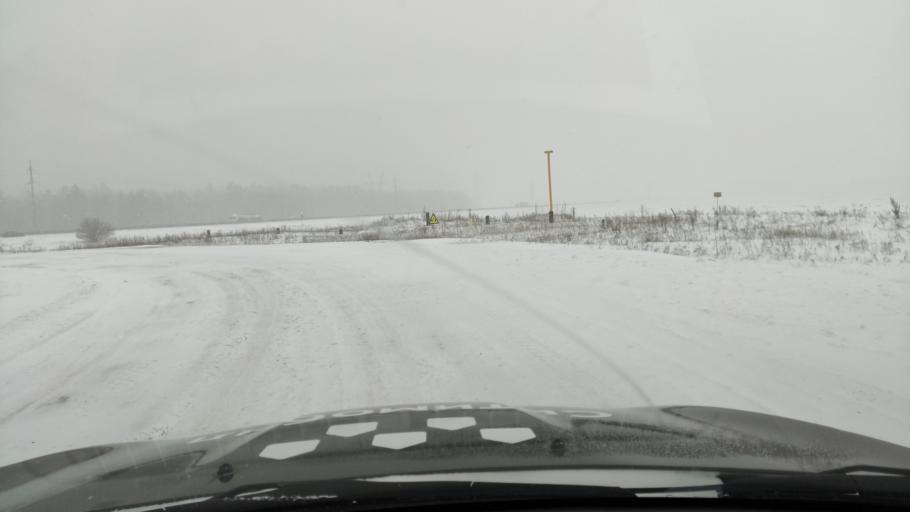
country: RU
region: Samara
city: Povolzhskiy
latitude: 53.5171
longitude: 49.6856
